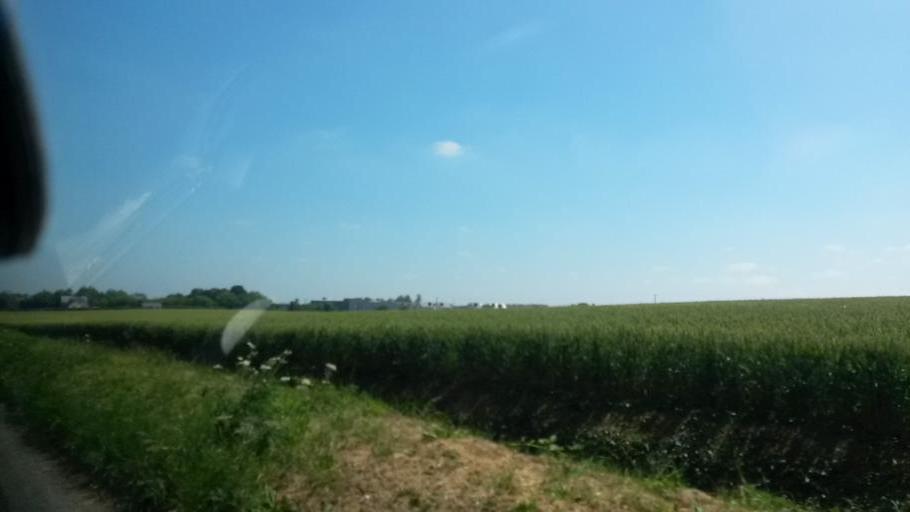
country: IE
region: Leinster
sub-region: Fingal County
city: Swords
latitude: 53.5207
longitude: -6.2754
